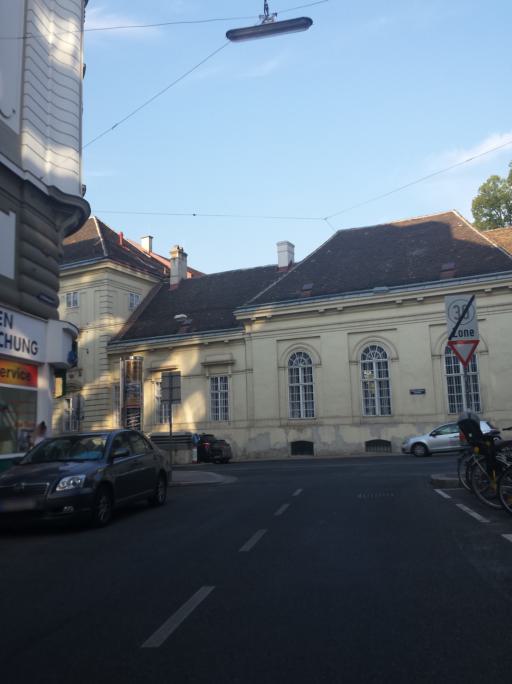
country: AT
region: Vienna
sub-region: Wien Stadt
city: Vienna
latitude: 48.1919
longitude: 16.3709
